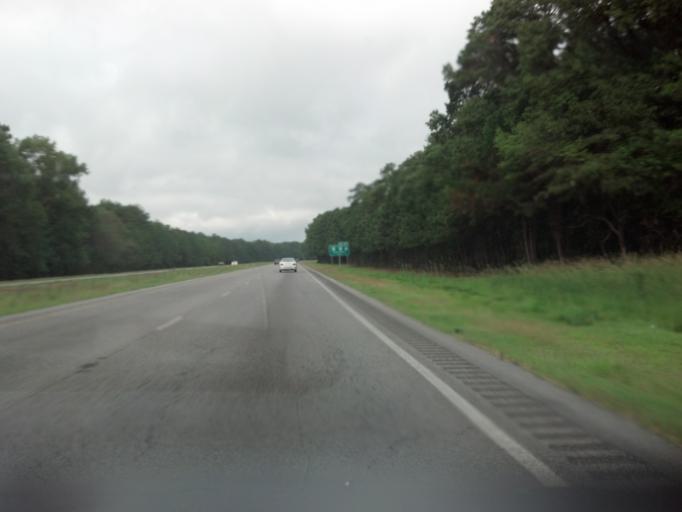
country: US
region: North Carolina
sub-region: Nash County
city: Rocky Mount
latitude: 35.9360
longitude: -77.7379
